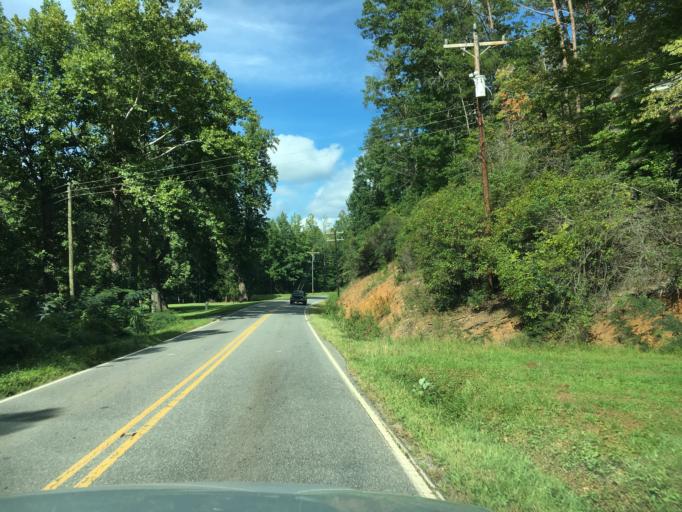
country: US
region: North Carolina
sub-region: Polk County
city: Columbus
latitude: 35.2872
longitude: -82.1761
